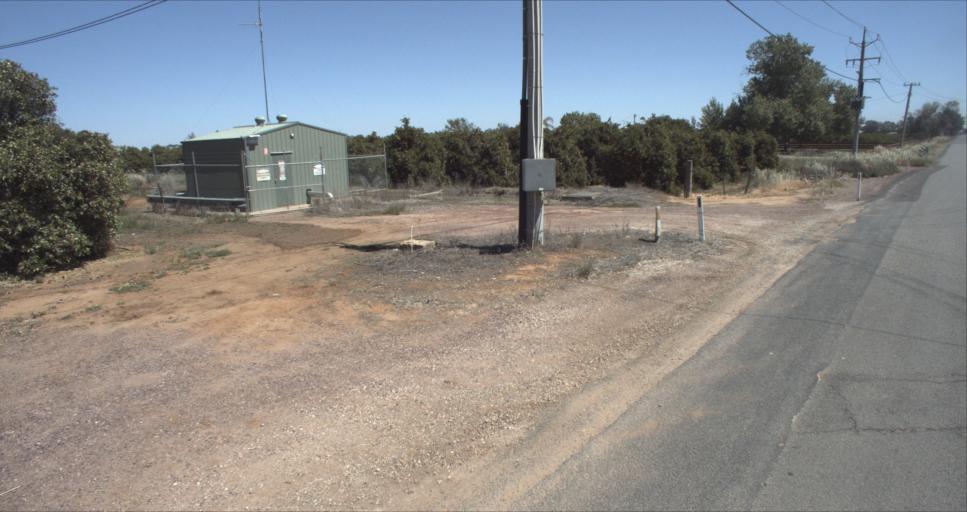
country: AU
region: New South Wales
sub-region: Leeton
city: Leeton
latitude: -34.5330
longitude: 146.3965
